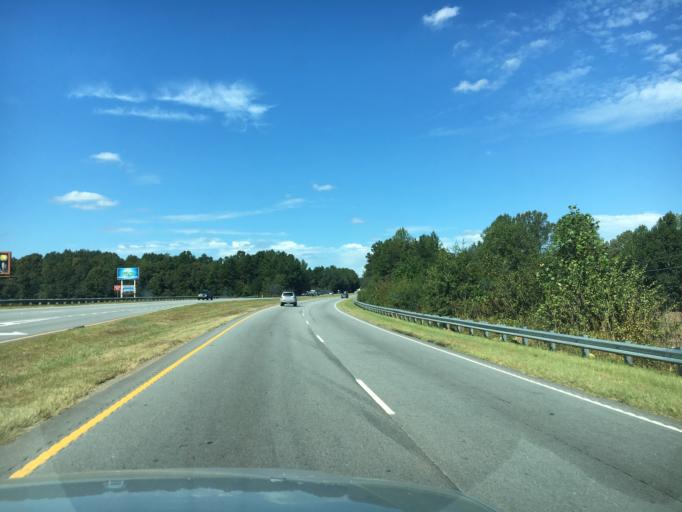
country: US
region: South Carolina
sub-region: Anderson County
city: Powdersville
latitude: 34.7985
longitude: -82.5098
